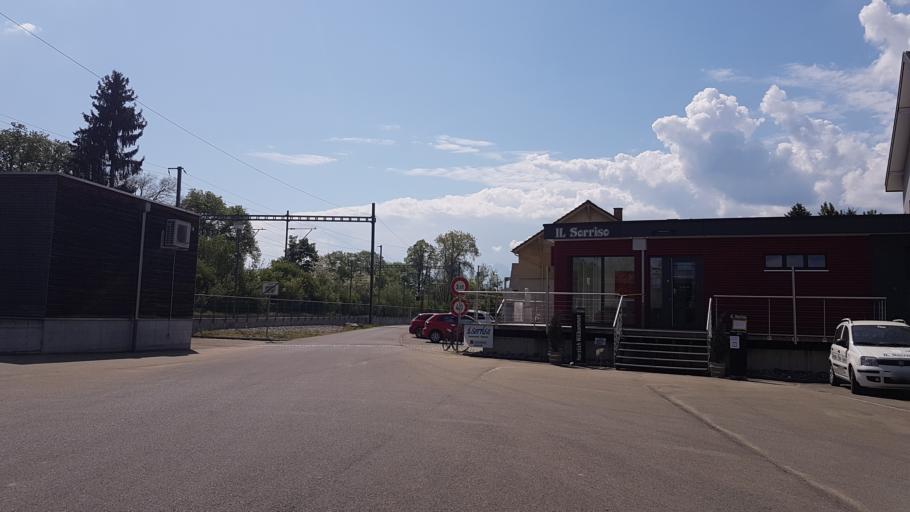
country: CH
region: Bern
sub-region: Bern-Mittelland District
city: Toffen
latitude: 46.8585
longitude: 7.4959
